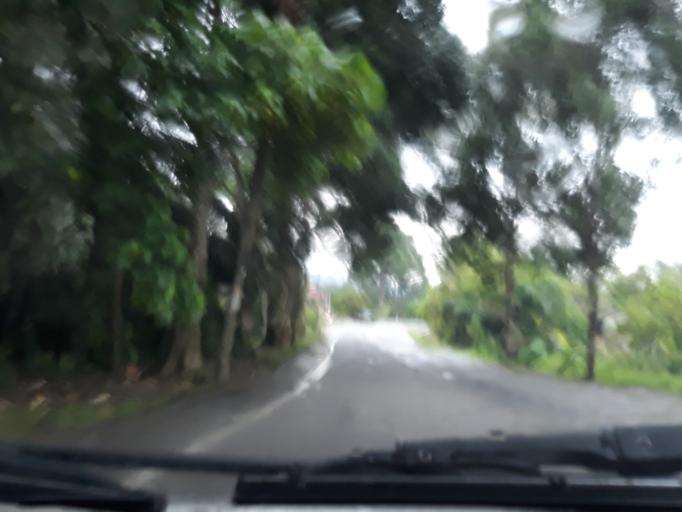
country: MY
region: Penang
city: Nibong Tebal
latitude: 5.2165
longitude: 100.6105
